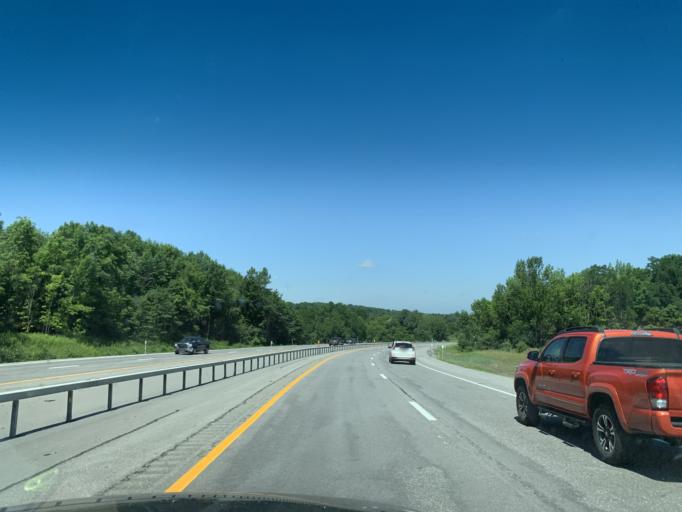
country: US
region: New York
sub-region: Oneida County
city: Chadwicks
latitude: 43.0322
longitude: -75.2688
